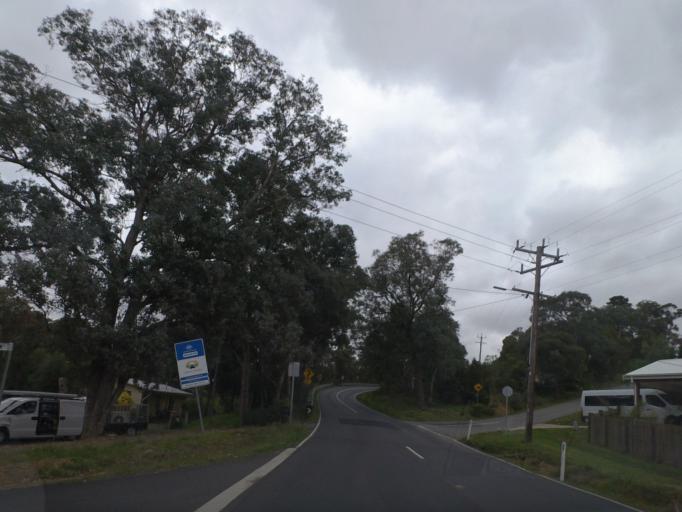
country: AU
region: Victoria
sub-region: Nillumbik
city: Diamond Creek
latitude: -37.6685
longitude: 145.1487
